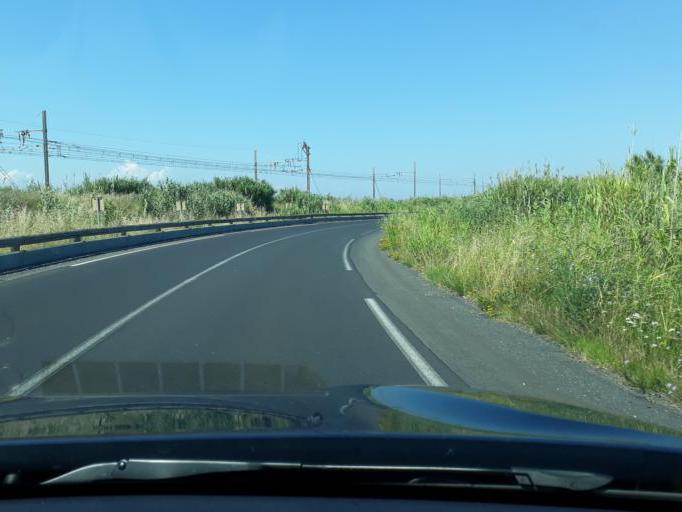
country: FR
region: Languedoc-Roussillon
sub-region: Departement de l'Herault
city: Marseillan
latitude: 43.3423
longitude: 3.5777
